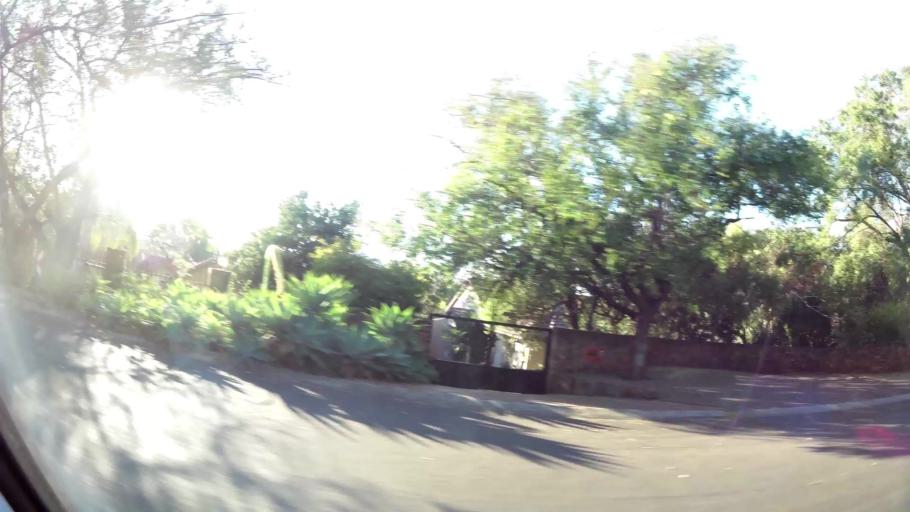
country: ZA
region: North-West
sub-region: Bojanala Platinum District Municipality
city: Rustenburg
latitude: -25.6892
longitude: 27.2071
